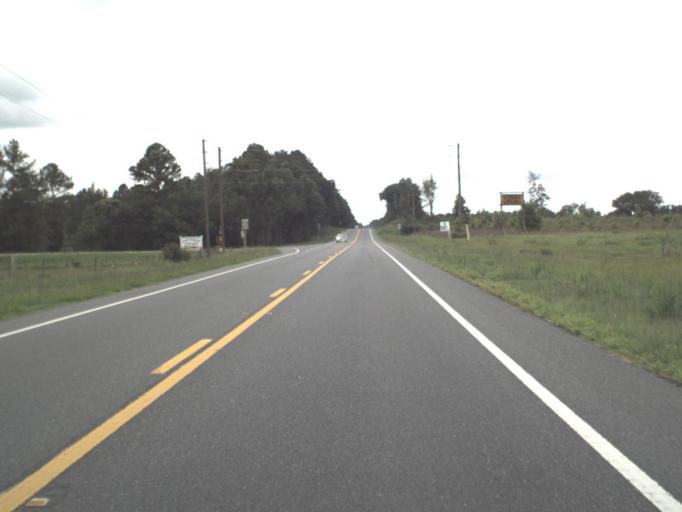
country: US
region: Florida
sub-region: Levy County
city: Williston Highlands
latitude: 29.2506
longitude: -82.4415
